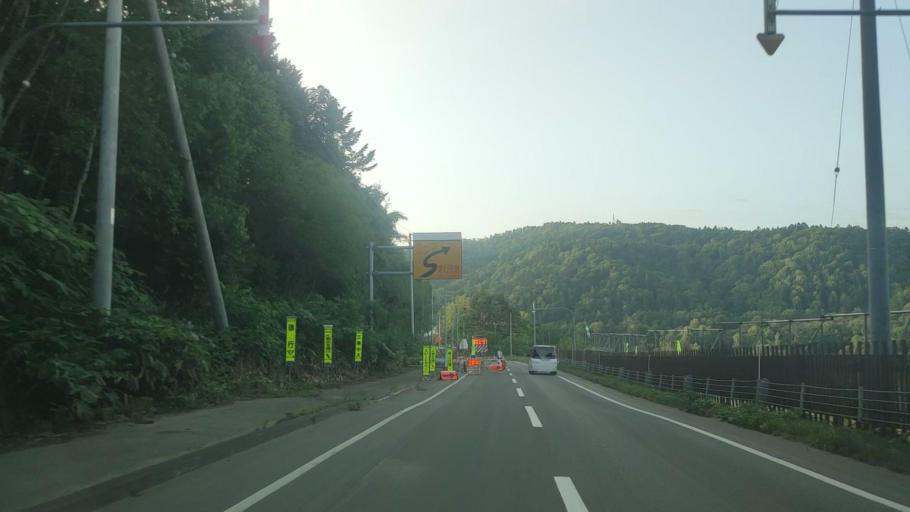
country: JP
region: Hokkaido
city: Bibai
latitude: 43.2314
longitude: 142.0394
